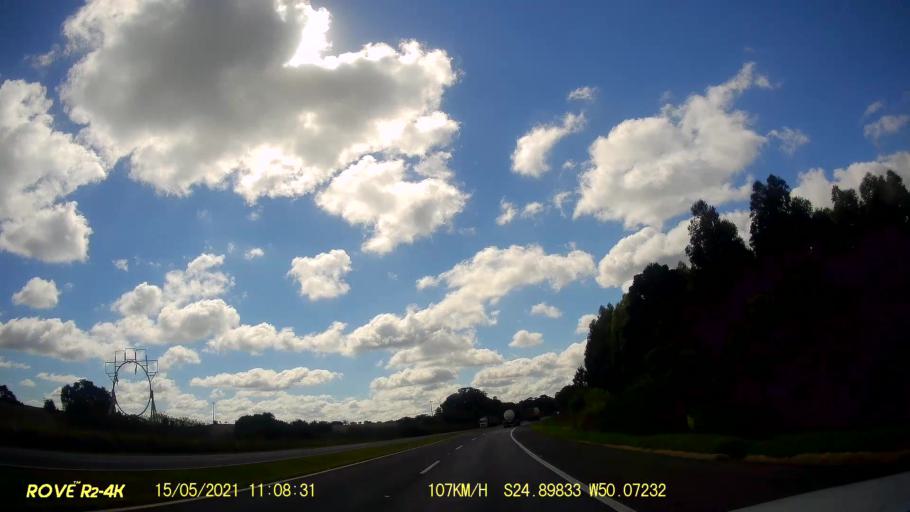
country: BR
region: Parana
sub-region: Carambei
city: Carambei
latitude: -24.8982
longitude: -50.0722
